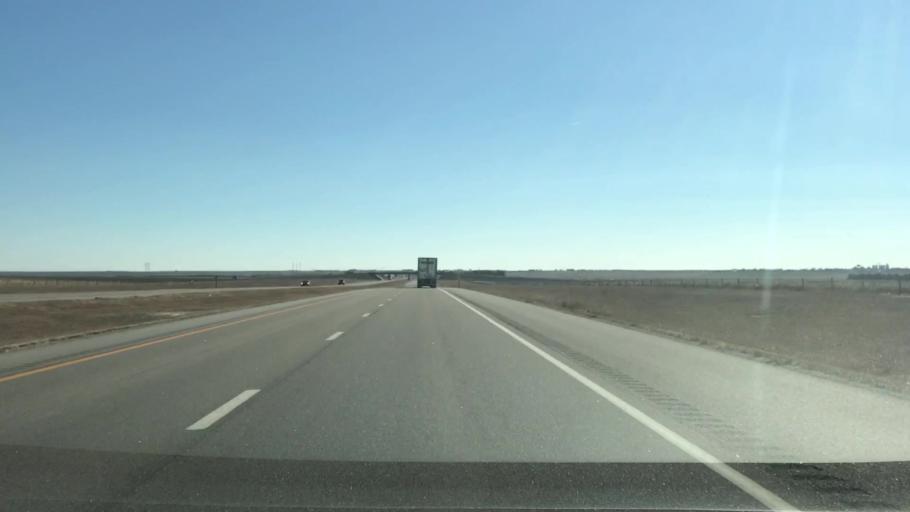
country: US
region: Kansas
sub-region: Logan County
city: Oakley
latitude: 39.1690
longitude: -100.8501
